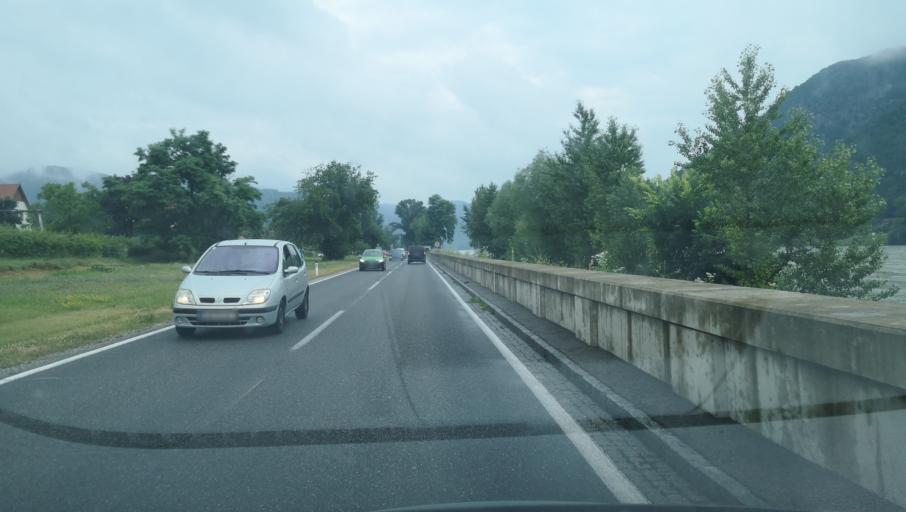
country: AT
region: Lower Austria
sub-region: Politischer Bezirk Krems
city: Weinzierl am Walde
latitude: 48.3835
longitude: 15.4592
